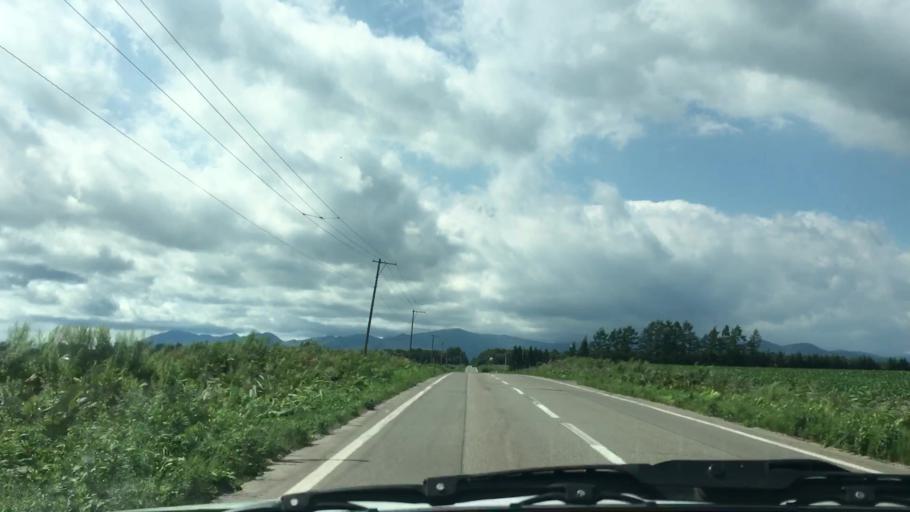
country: JP
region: Hokkaido
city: Otofuke
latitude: 43.2757
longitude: 143.3774
